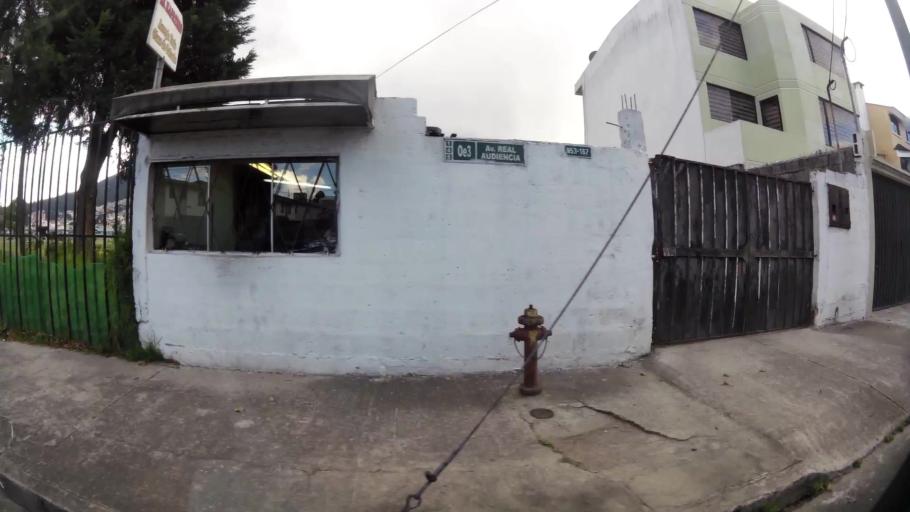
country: EC
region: Pichincha
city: Quito
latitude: -0.1395
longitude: -78.4860
